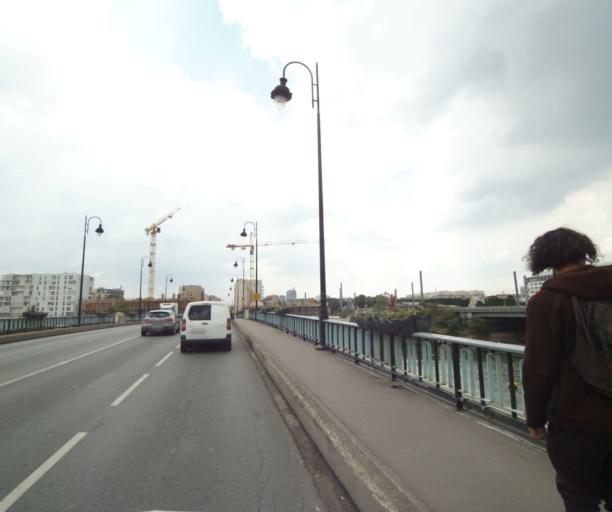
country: FR
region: Ile-de-France
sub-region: Departement des Hauts-de-Seine
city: Levallois-Perret
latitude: 48.9045
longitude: 2.2883
